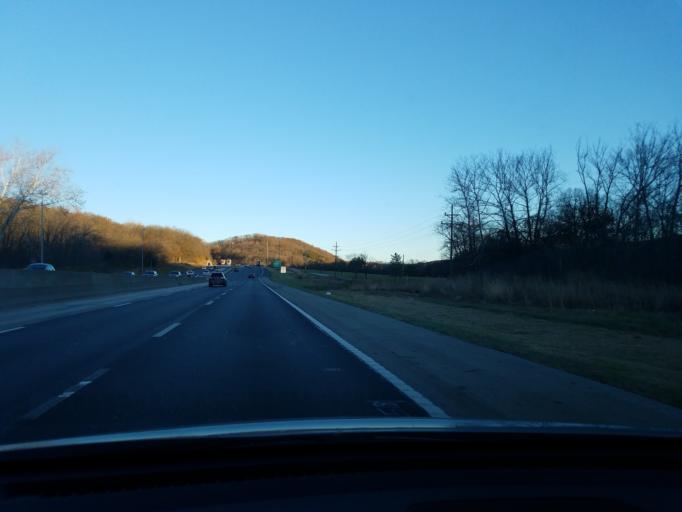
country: US
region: Missouri
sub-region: Jefferson County
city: High Ridge
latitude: 38.5076
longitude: -90.5679
